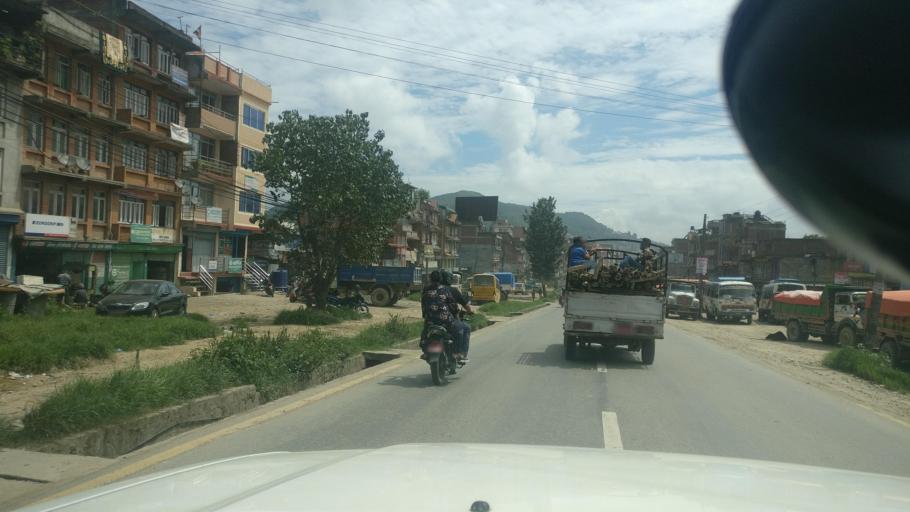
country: NP
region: Central Region
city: Banepa
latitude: 27.6323
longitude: 85.5125
